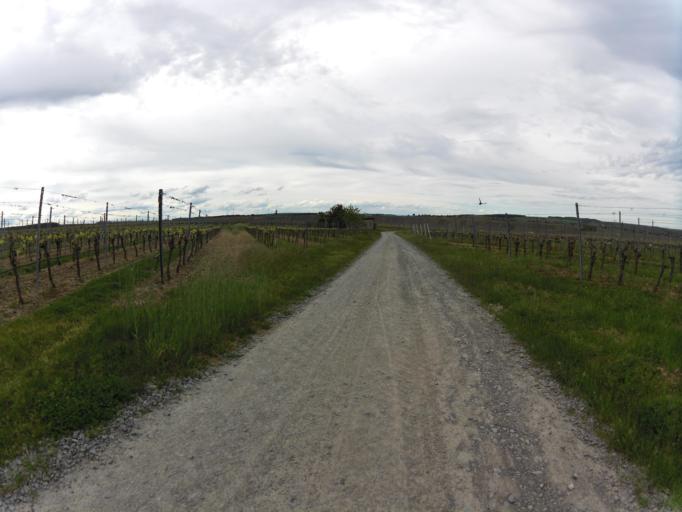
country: DE
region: Bavaria
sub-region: Regierungsbezirk Unterfranken
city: Nordheim
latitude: 49.8498
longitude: 10.1930
